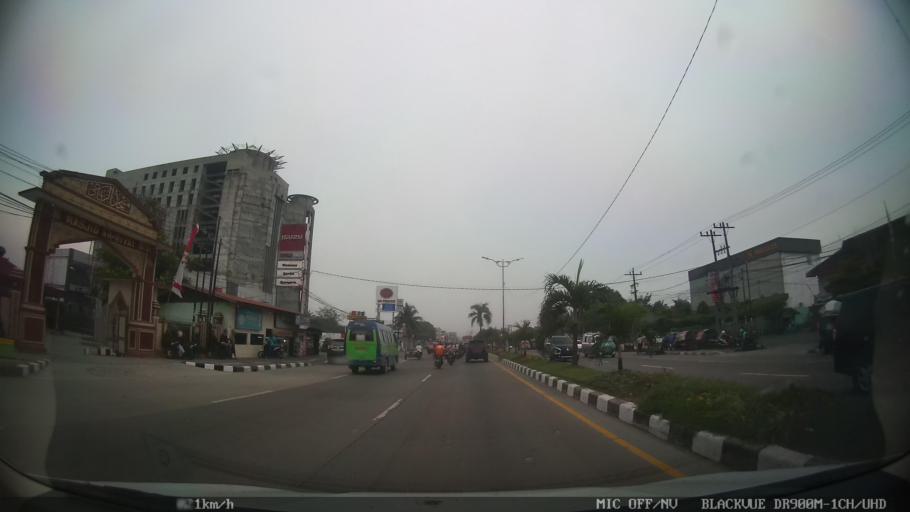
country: ID
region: North Sumatra
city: Deli Tua
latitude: 3.5383
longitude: 98.7058
